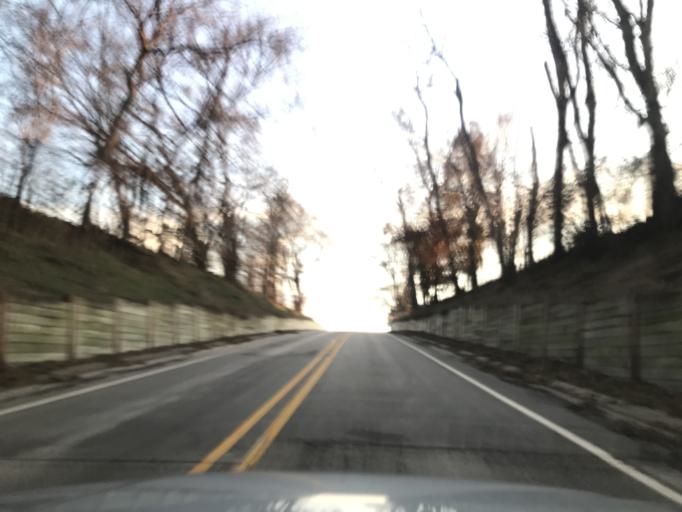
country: US
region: Illinois
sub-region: Henderson County
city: Oquawka
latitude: 40.9268
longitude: -90.8642
